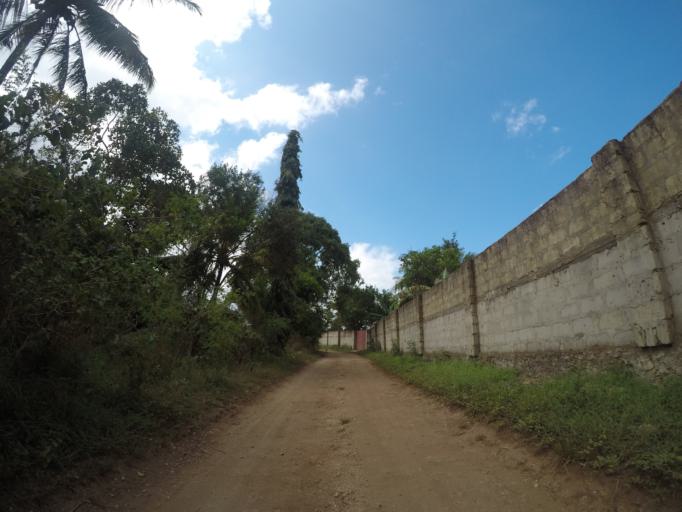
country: TZ
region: Zanzibar Central/South
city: Koani
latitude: -6.1944
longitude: 39.3167
